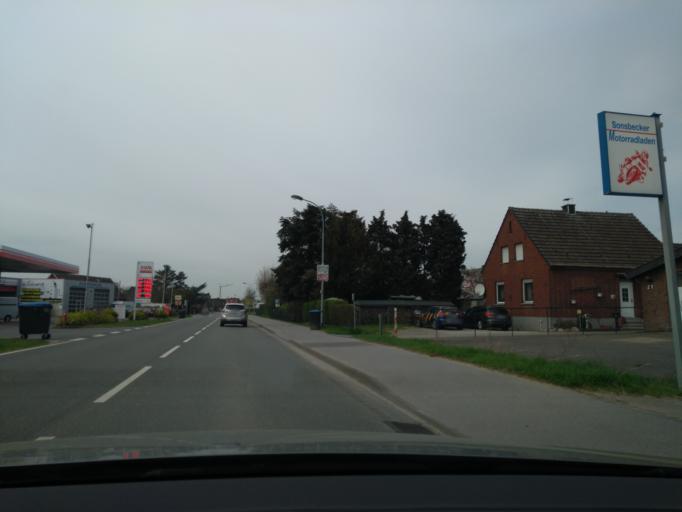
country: DE
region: North Rhine-Westphalia
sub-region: Regierungsbezirk Dusseldorf
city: Sonsbeck
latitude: 51.6007
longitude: 6.3843
